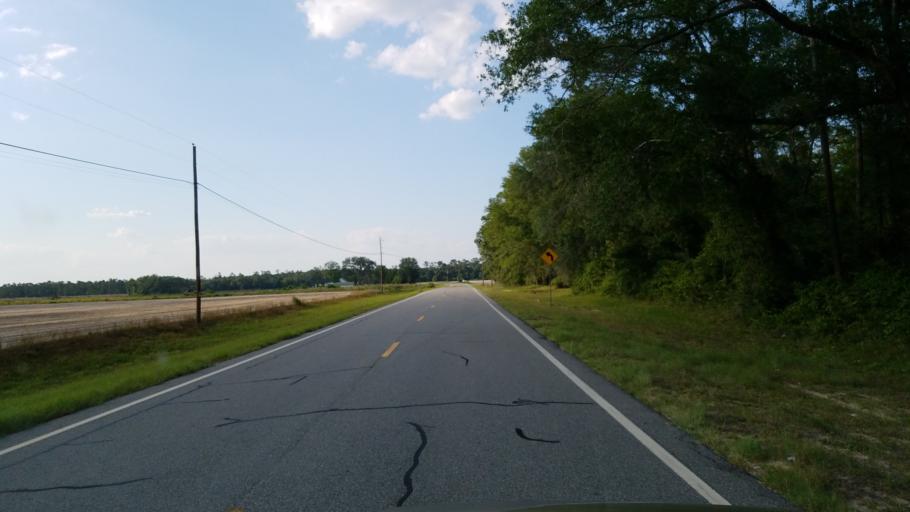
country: US
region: Georgia
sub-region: Echols County
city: Statenville
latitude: 30.7947
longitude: -83.0523
